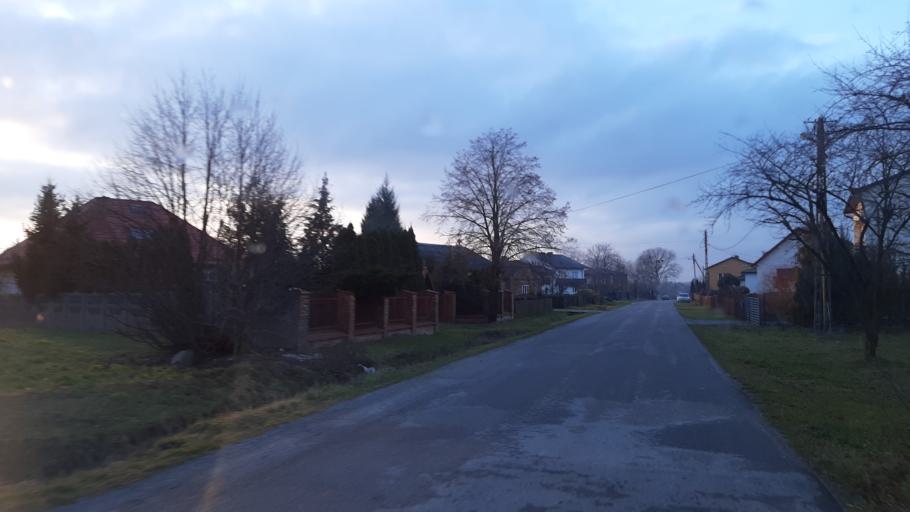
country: PL
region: Lublin Voivodeship
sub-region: Powiat lubelski
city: Garbow
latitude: 51.3808
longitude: 22.3958
